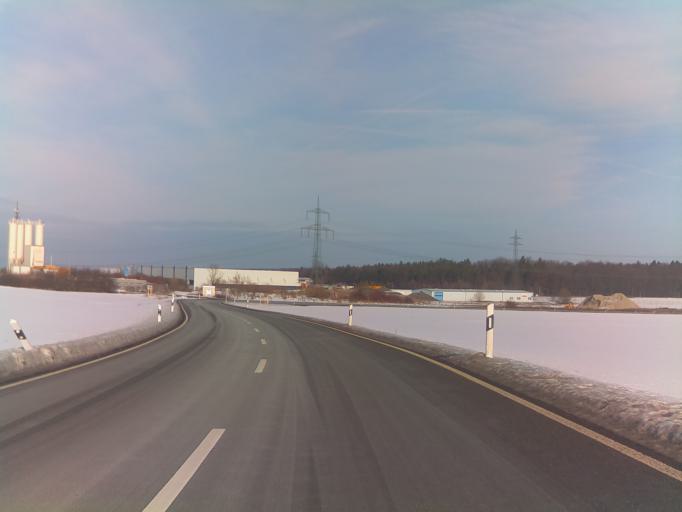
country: DE
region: Thuringia
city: Milda
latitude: 50.8722
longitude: 11.4609
